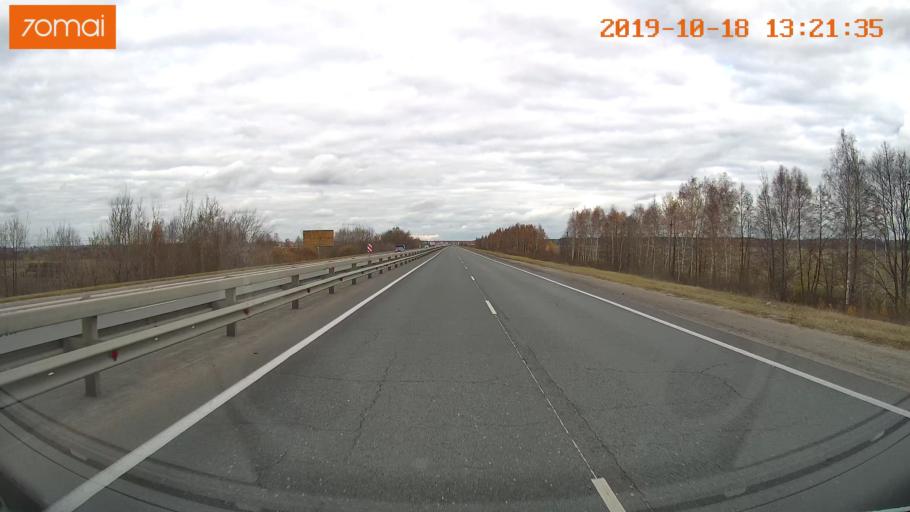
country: RU
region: Rjazan
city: Polyany
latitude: 54.6968
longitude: 39.8404
